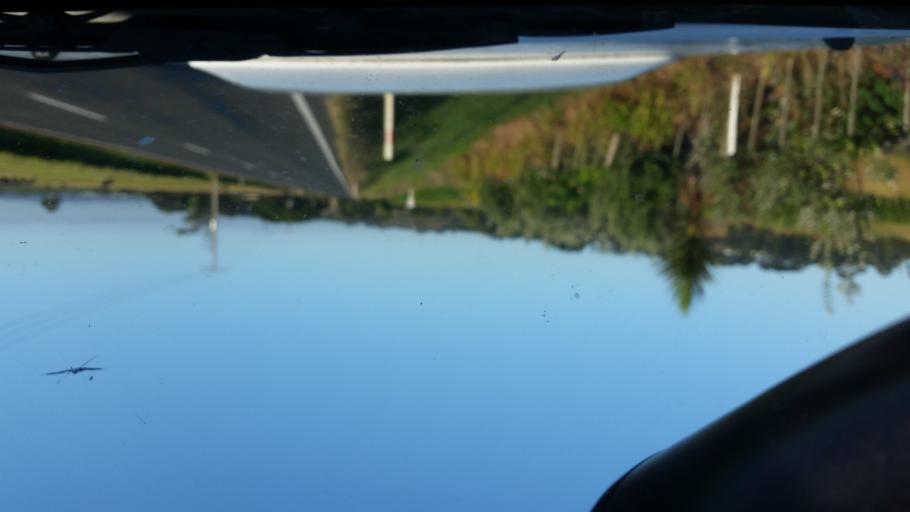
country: NZ
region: Northland
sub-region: Kaipara District
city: Dargaville
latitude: -35.9687
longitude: 173.8715
